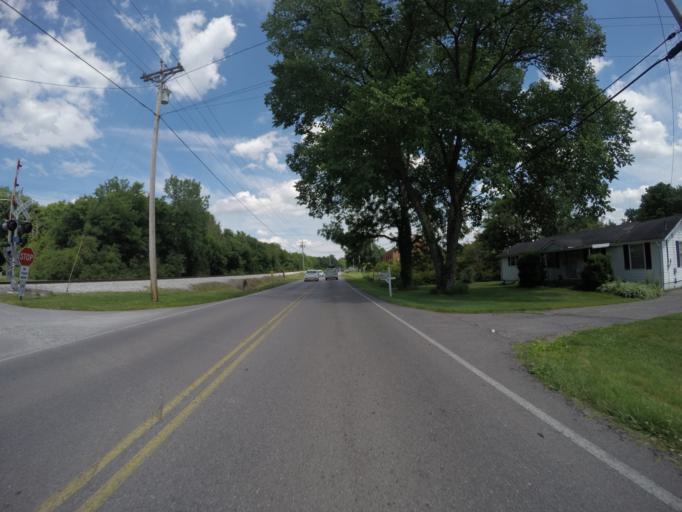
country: US
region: Tennessee
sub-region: Wilson County
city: Mount Juliet
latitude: 36.2041
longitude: -86.5295
